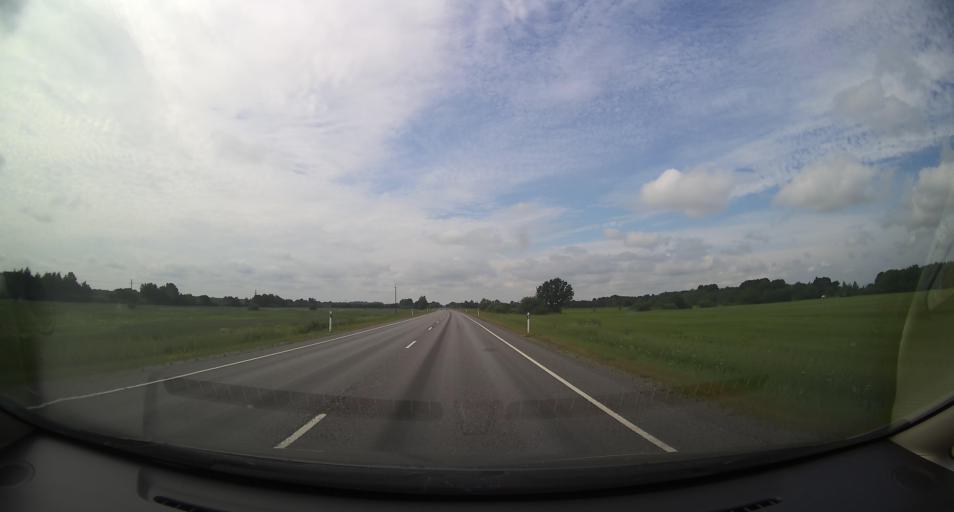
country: EE
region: Laeaene
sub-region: Lihula vald
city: Lihula
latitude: 58.7180
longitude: 23.8872
